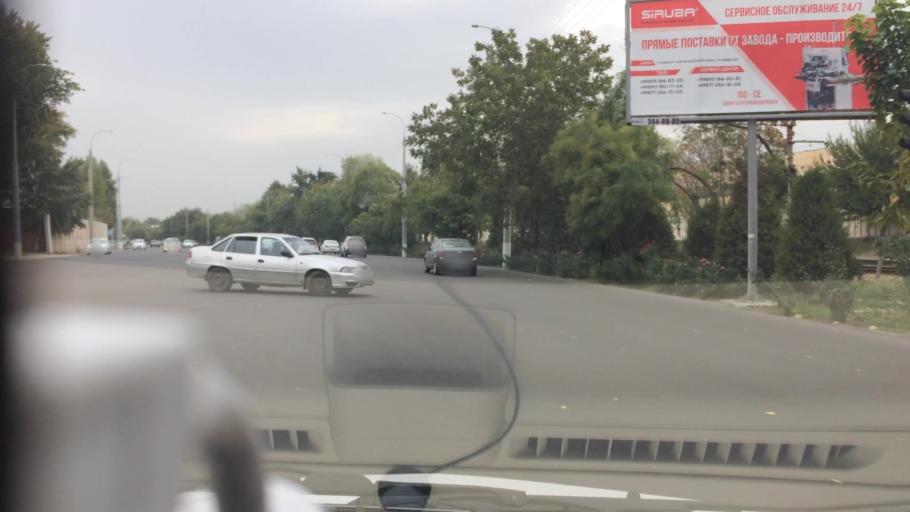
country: UZ
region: Toshkent
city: Salor
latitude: 41.3094
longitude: 69.3050
